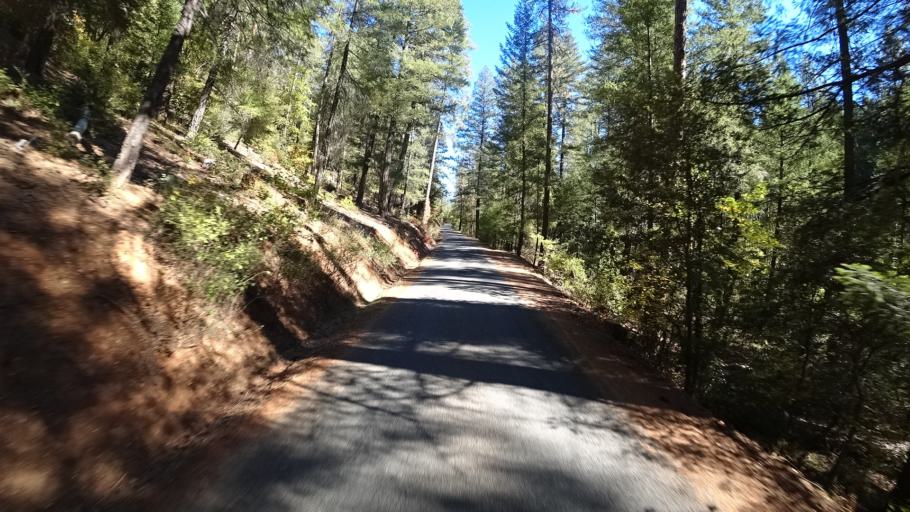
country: US
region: California
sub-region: Siskiyou County
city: Happy Camp
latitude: 41.3013
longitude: -123.1460
